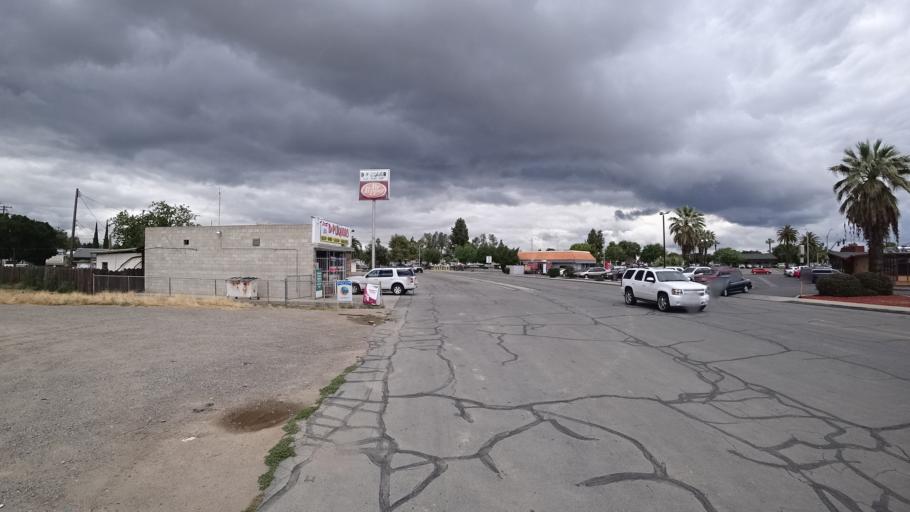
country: US
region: California
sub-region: Kings County
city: Hanford
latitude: 36.3271
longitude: -119.6587
